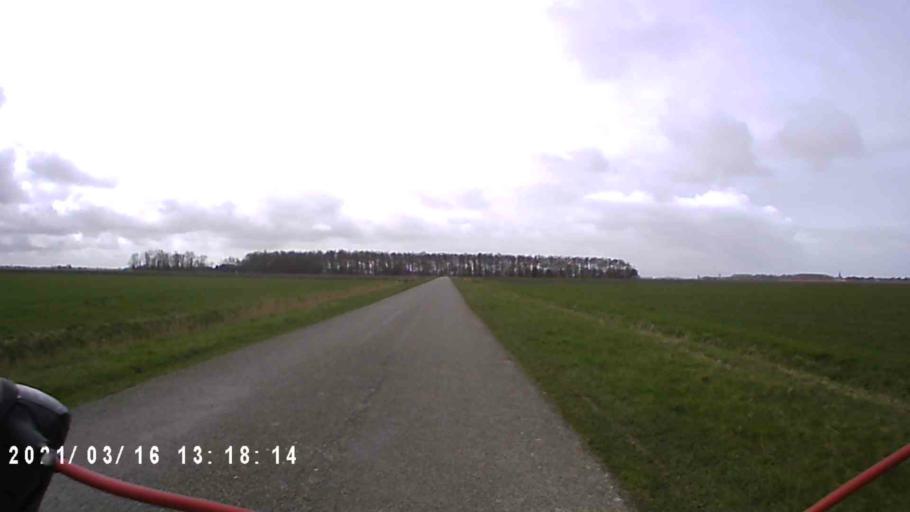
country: NL
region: Friesland
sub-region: Gemeente Het Bildt
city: Minnertsga
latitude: 53.2360
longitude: 5.5859
